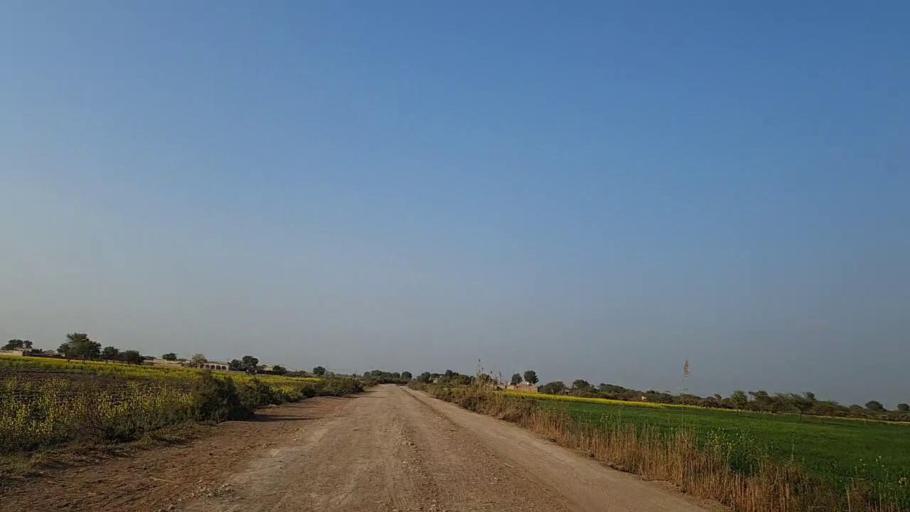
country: PK
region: Sindh
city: Sakrand
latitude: 26.1104
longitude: 68.3689
